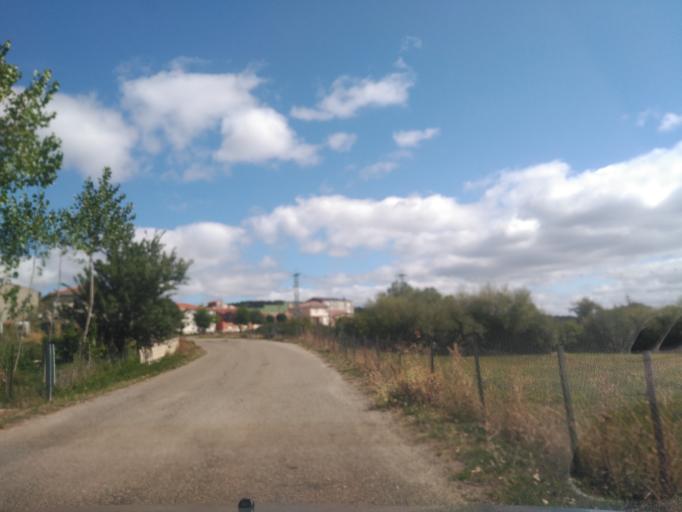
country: ES
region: Castille and Leon
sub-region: Provincia de Soria
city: Espejon
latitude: 41.8525
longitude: -3.2265
